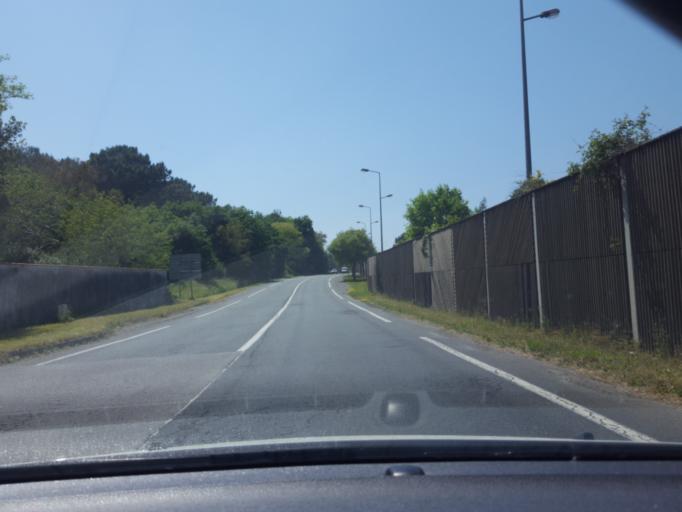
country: FR
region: Aquitaine
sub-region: Departement des Landes
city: Tarnos
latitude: 43.5524
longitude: -1.4642
